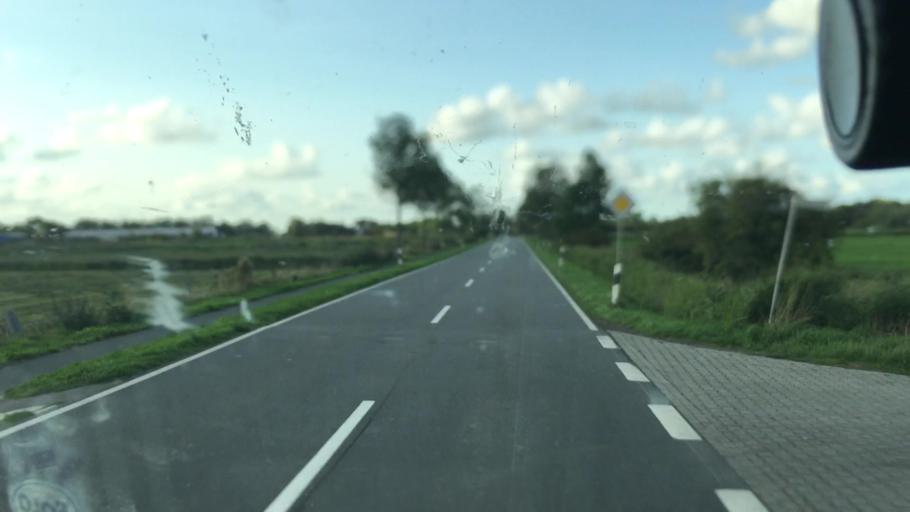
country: DE
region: Lower Saxony
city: Jever
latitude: 53.5859
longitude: 7.8768
